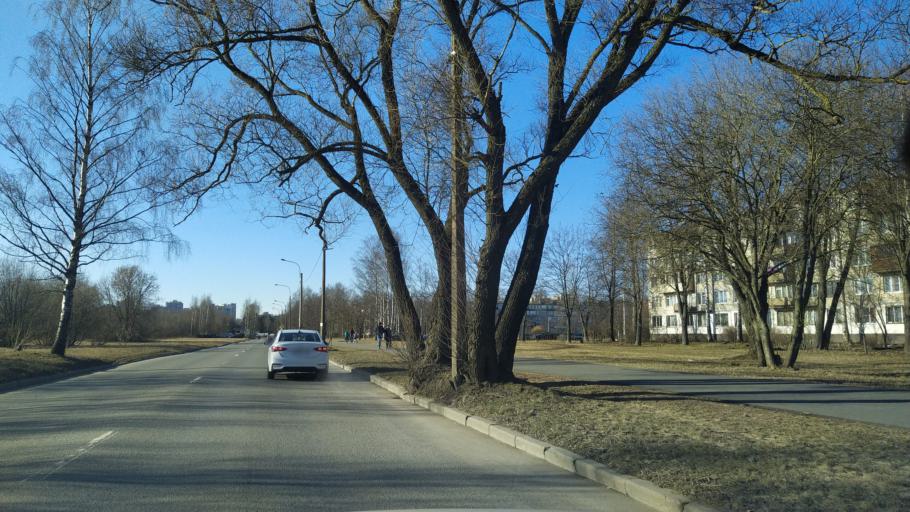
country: RU
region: Leningrad
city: Akademicheskoe
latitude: 59.9990
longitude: 30.4291
